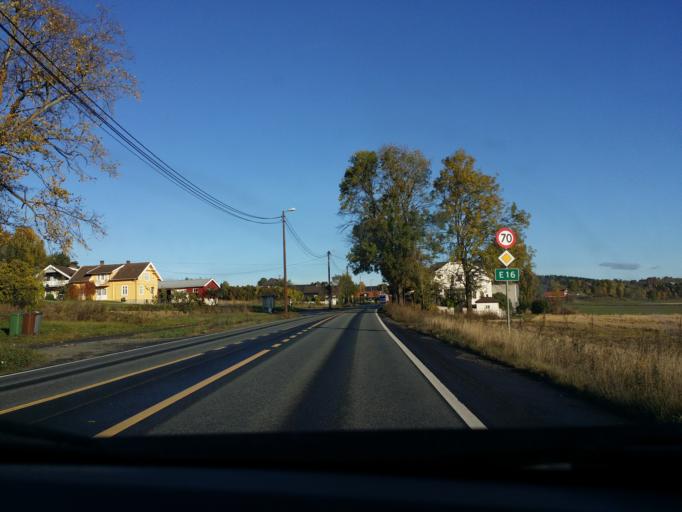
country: NO
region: Buskerud
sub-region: Hole
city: Vik
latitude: 60.1157
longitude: 10.2841
